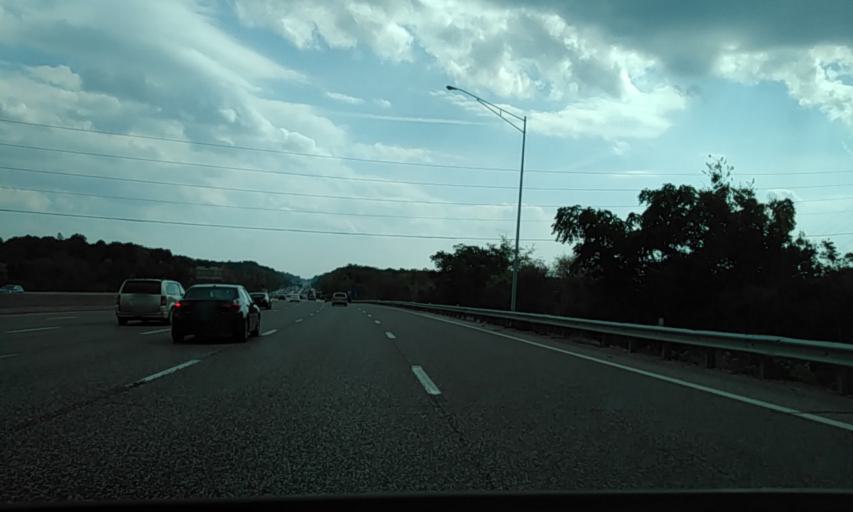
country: US
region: Missouri
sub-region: Saint Louis County
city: Sunset Hills
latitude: 38.5432
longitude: -90.4222
